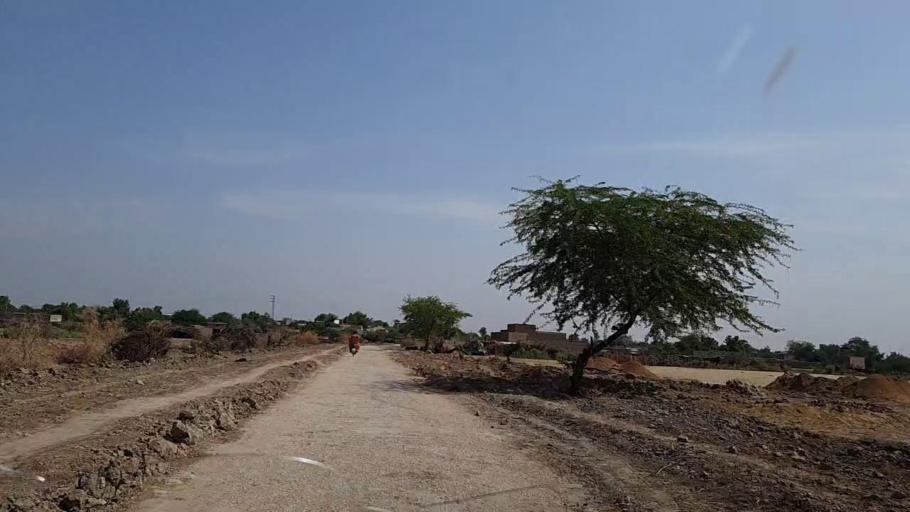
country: PK
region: Sindh
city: Khanpur
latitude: 27.7522
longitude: 69.3374
